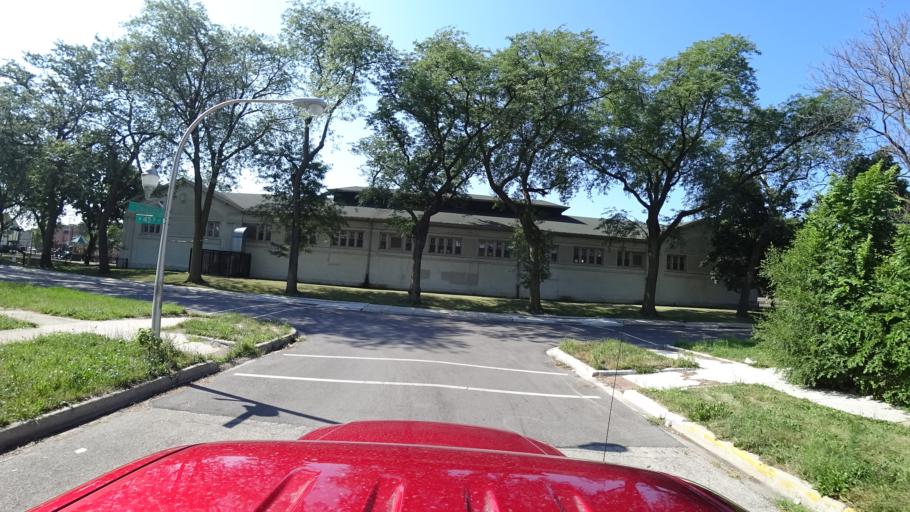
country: US
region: Illinois
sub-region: Cook County
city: Chicago
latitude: 41.8127
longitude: -87.6347
